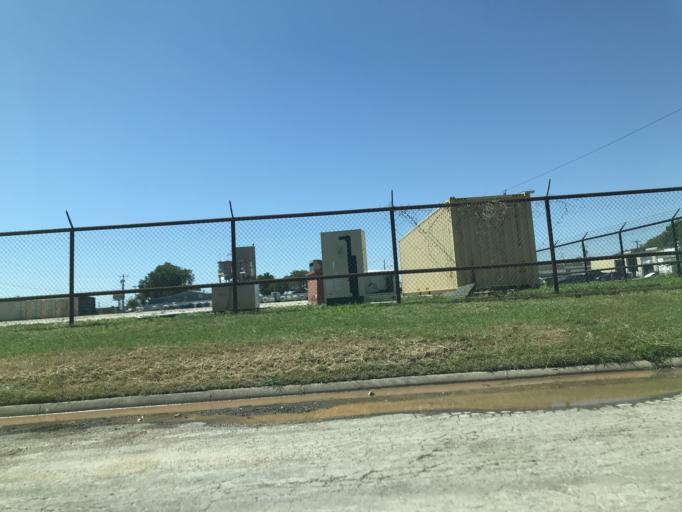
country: US
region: Texas
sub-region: Taylor County
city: Abilene
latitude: 32.4231
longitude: -99.7384
